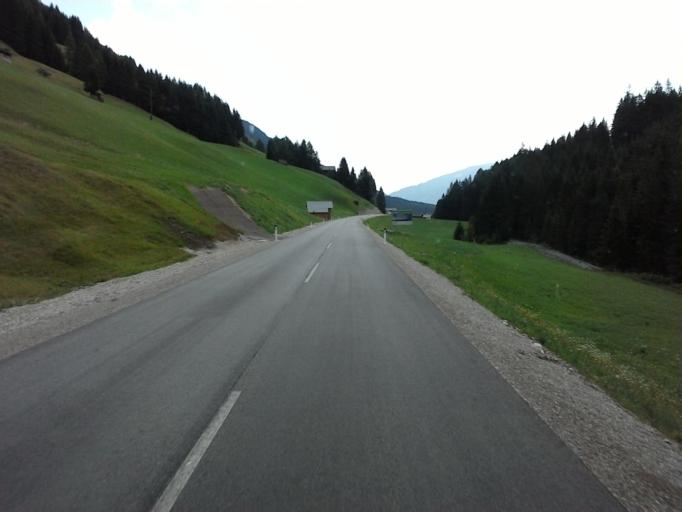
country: AT
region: Tyrol
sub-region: Politischer Bezirk Lienz
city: Abfaltersbach
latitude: 46.7165
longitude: 12.5510
